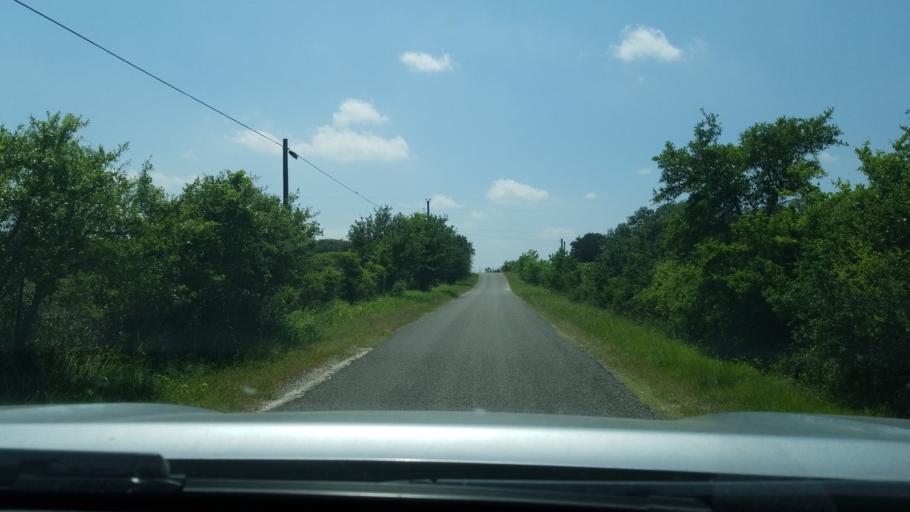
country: US
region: Texas
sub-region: Blanco County
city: Blanco
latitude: 29.9903
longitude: -98.5304
